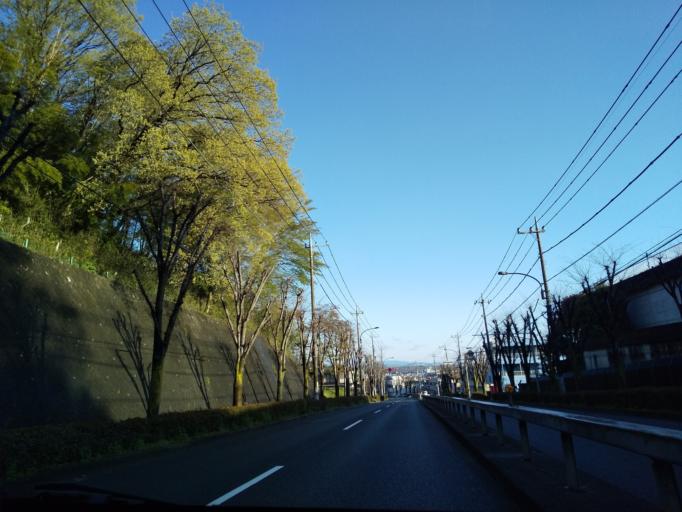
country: JP
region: Tokyo
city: Hachioji
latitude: 35.6343
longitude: 139.3634
